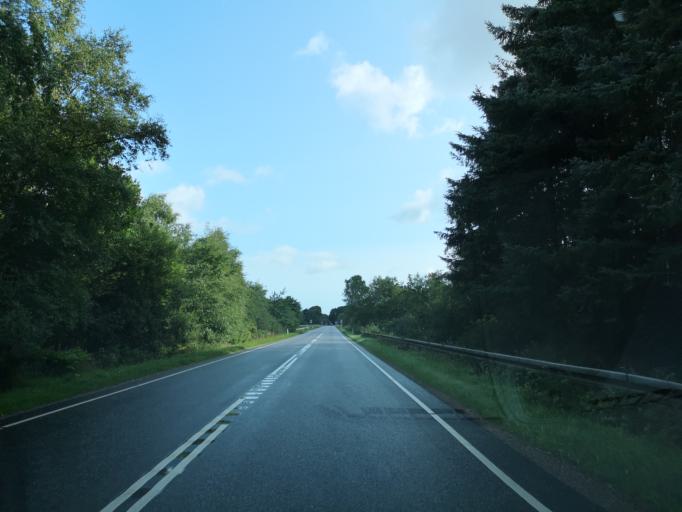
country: DK
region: Central Jutland
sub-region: Ringkobing-Skjern Kommune
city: Videbaek
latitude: 56.0406
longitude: 8.6145
